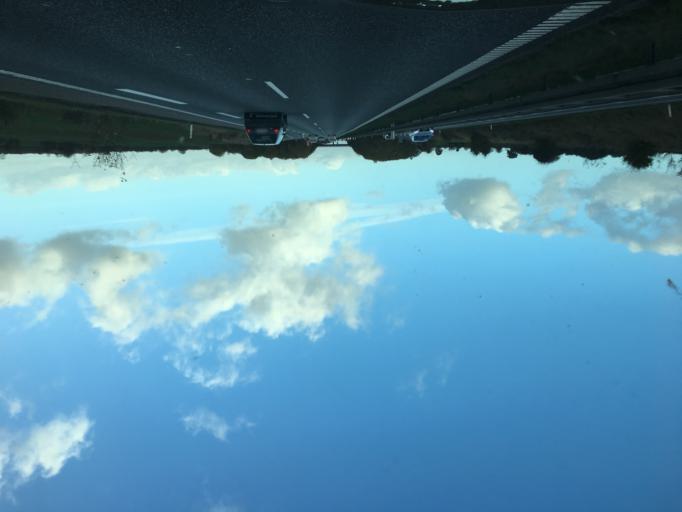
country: DK
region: South Denmark
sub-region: Kolding Kommune
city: Christiansfeld
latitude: 55.3554
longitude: 9.4474
